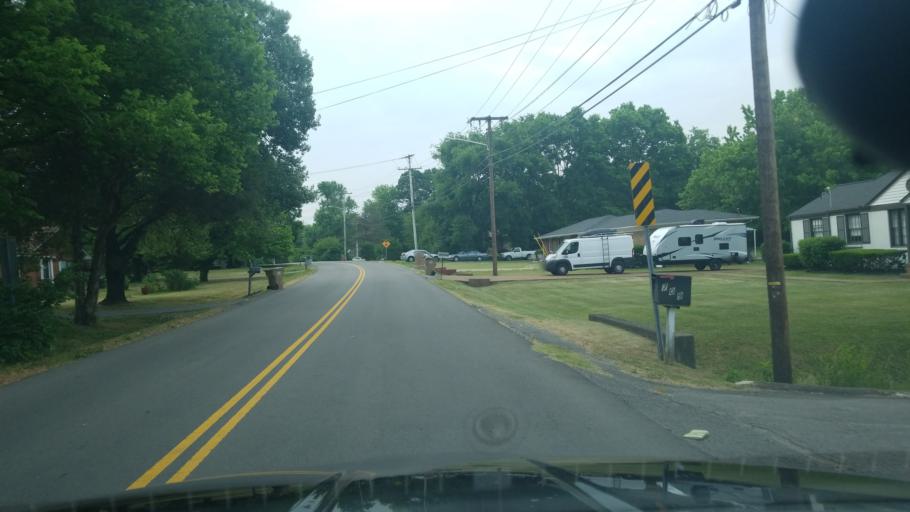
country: US
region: Tennessee
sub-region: Davidson County
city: Goodlettsville
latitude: 36.2644
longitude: -86.7446
